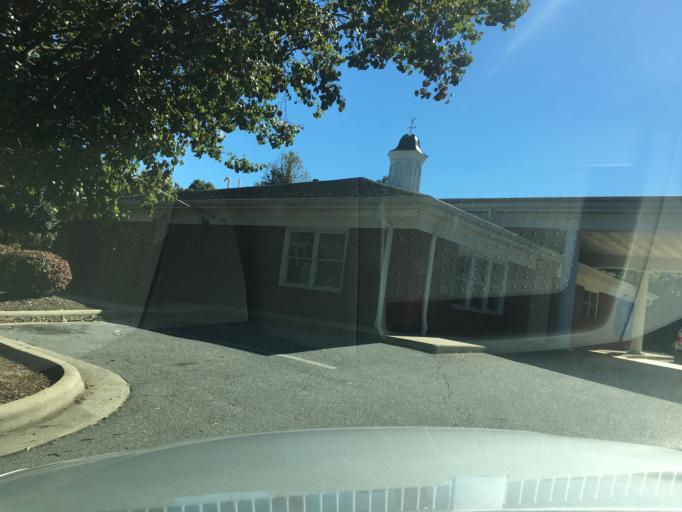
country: US
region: North Carolina
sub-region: Catawba County
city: Conover
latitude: 35.7128
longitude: -81.2646
